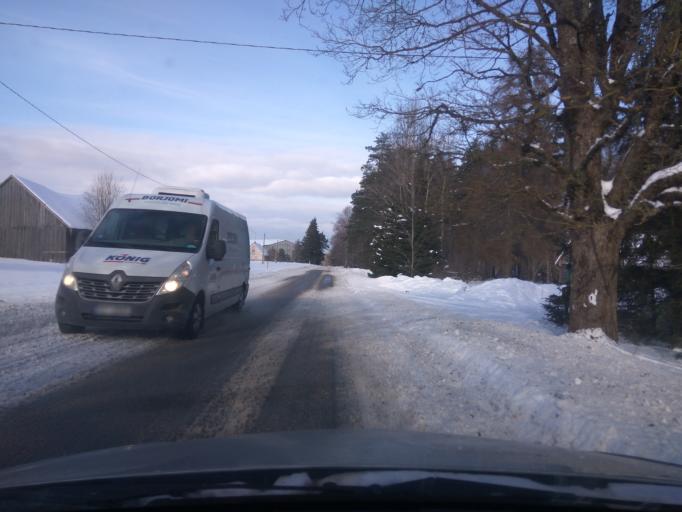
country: LV
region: Ventspils Rajons
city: Piltene
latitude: 57.3991
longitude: 21.8658
